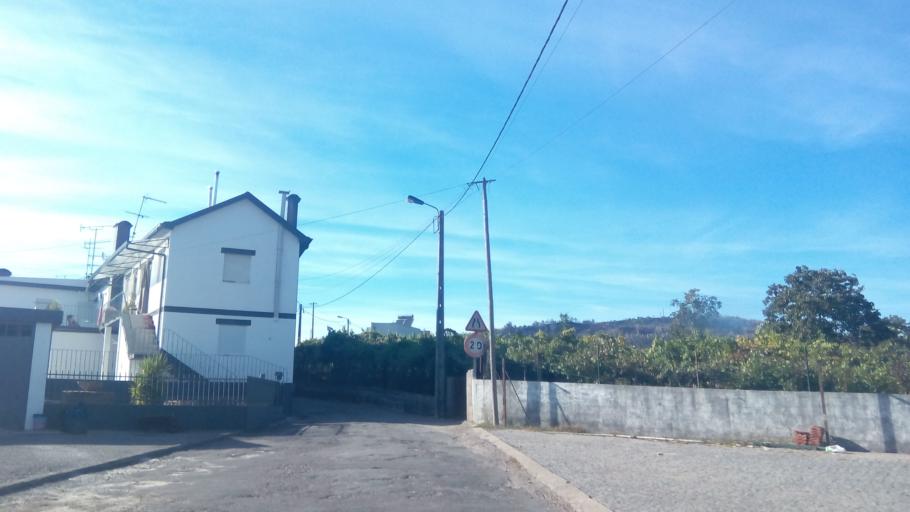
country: PT
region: Porto
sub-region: Paredes
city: Baltar
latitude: 41.1814
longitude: -8.3803
